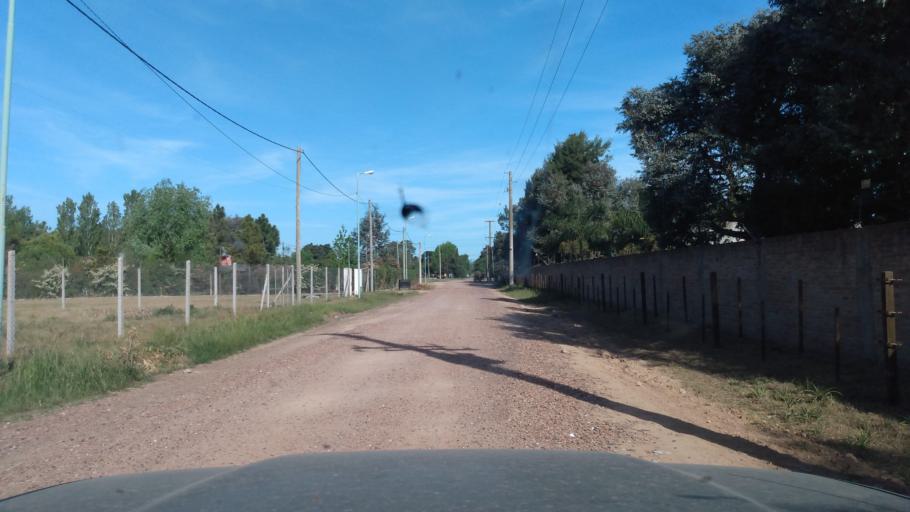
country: AR
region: Buenos Aires
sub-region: Partido de Lujan
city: Lujan
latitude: -34.5951
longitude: -59.1430
